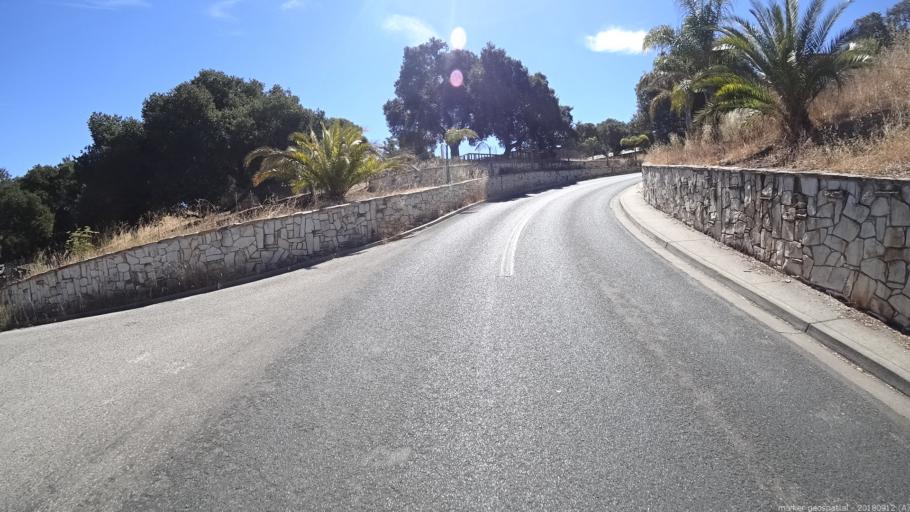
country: US
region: California
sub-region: Monterey County
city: Carmel Valley Village
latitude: 36.4700
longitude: -121.7277
